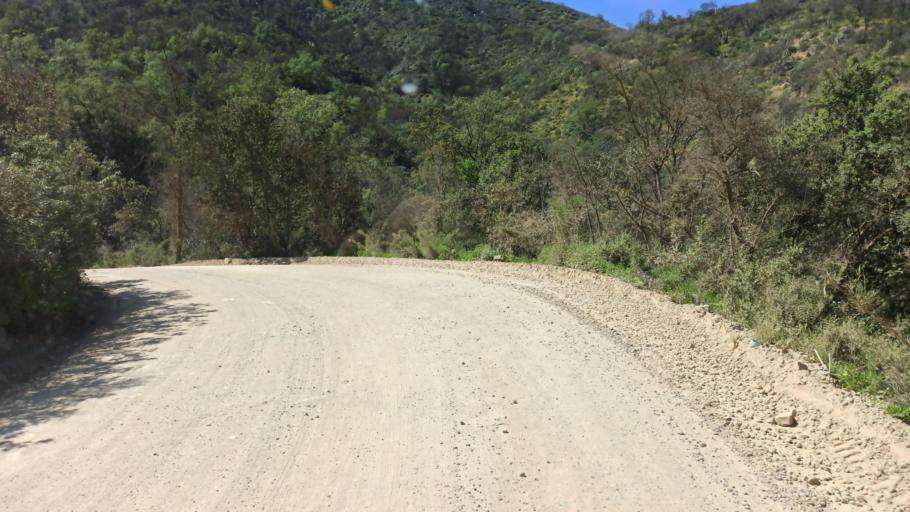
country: CL
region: Valparaiso
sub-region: Provincia de Marga Marga
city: Limache
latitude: -33.1985
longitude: -71.2651
